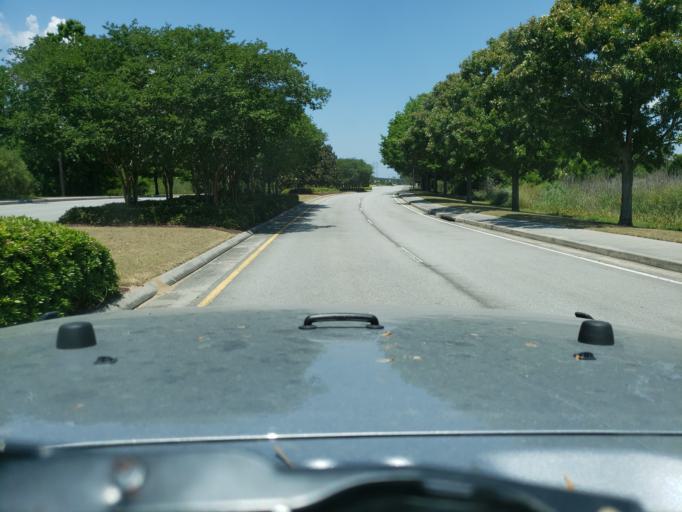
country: US
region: Georgia
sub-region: Chatham County
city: Savannah
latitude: 32.0906
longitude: -81.0891
